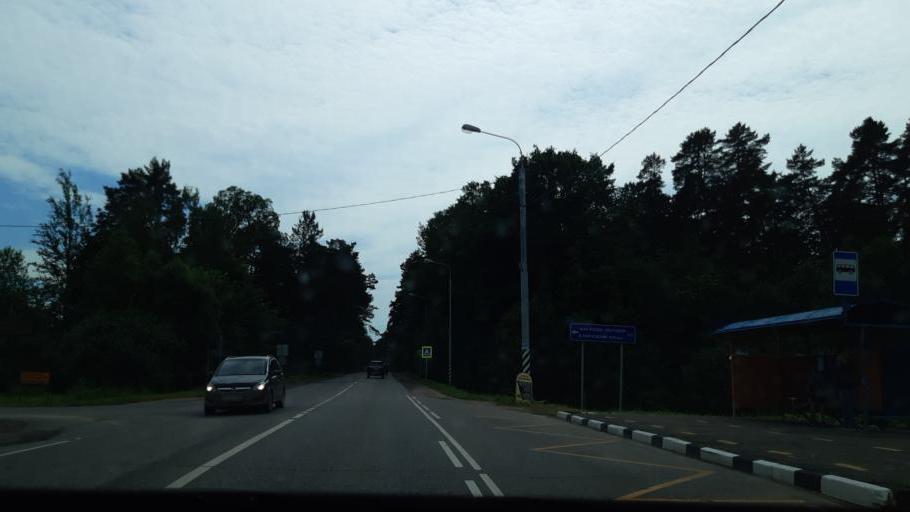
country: RU
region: Moskovskaya
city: Vereya
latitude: 55.3582
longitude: 36.2045
